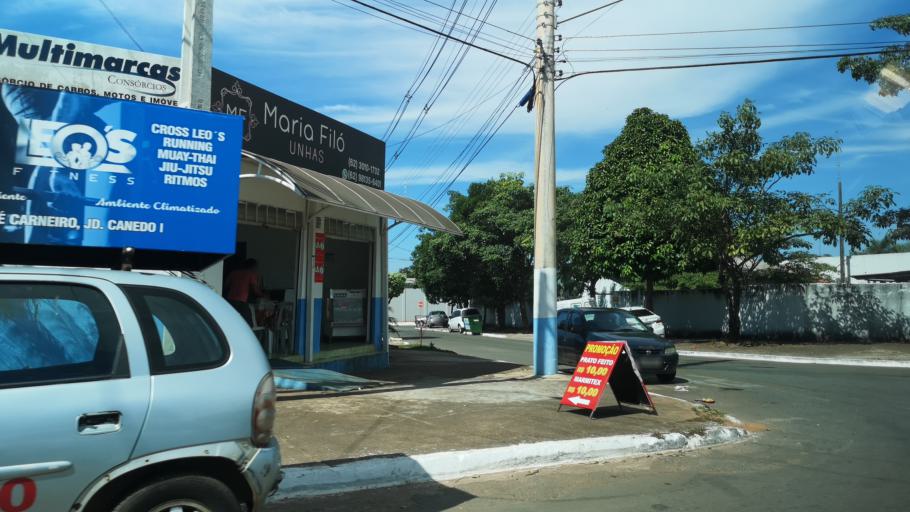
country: BR
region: Goias
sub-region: Senador Canedo
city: Senador Canedo
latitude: -16.7013
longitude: -49.1043
